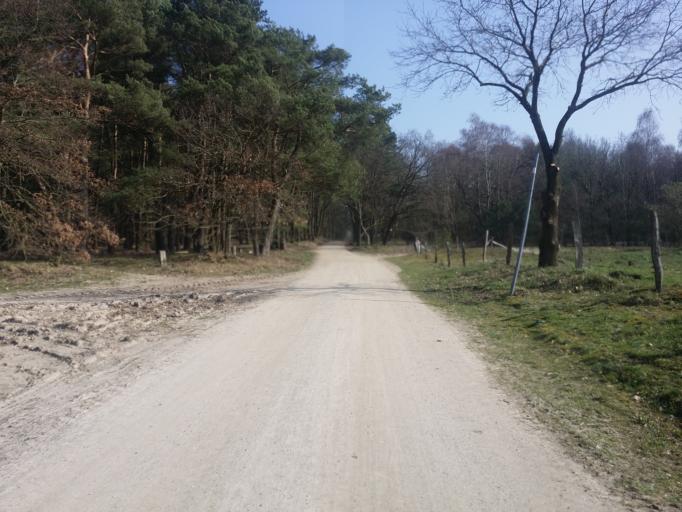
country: DE
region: Lower Saxony
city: Delmenhorst
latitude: 53.0136
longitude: 8.6756
